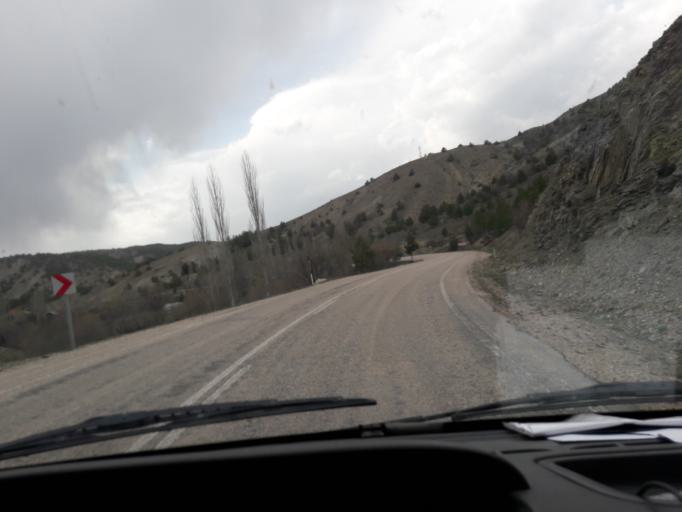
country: TR
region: Giresun
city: Alucra
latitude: 40.2751
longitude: 38.8282
